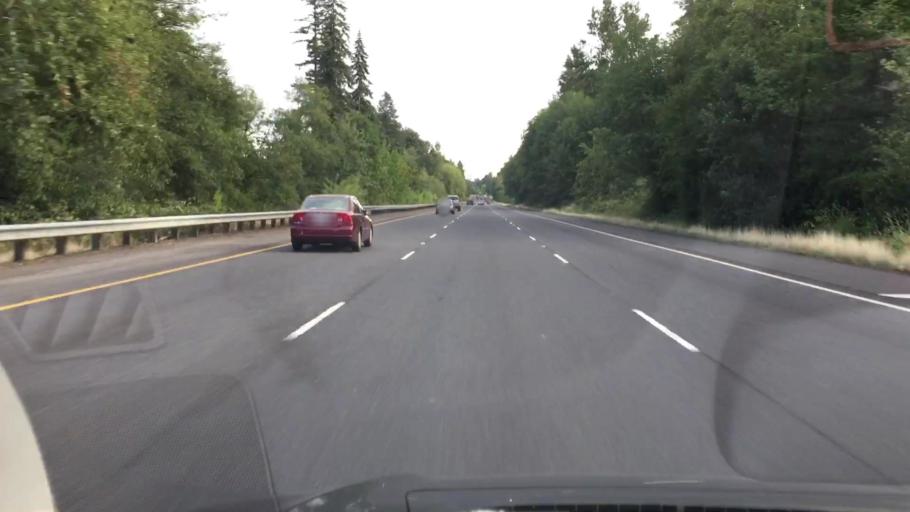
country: US
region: Washington
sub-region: Cowlitz County
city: West Side Highway
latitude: 46.2252
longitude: -122.8897
